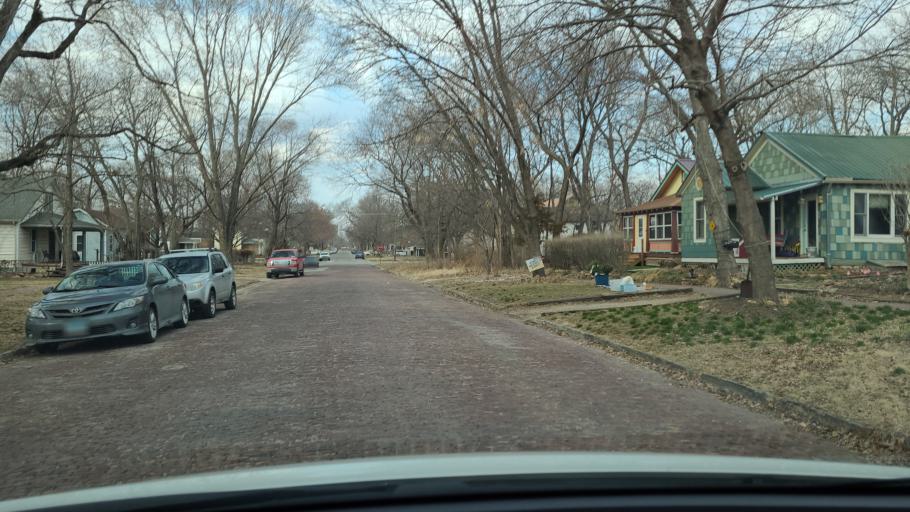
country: US
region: Kansas
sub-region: Douglas County
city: Lawrence
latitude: 38.9684
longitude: -95.2312
